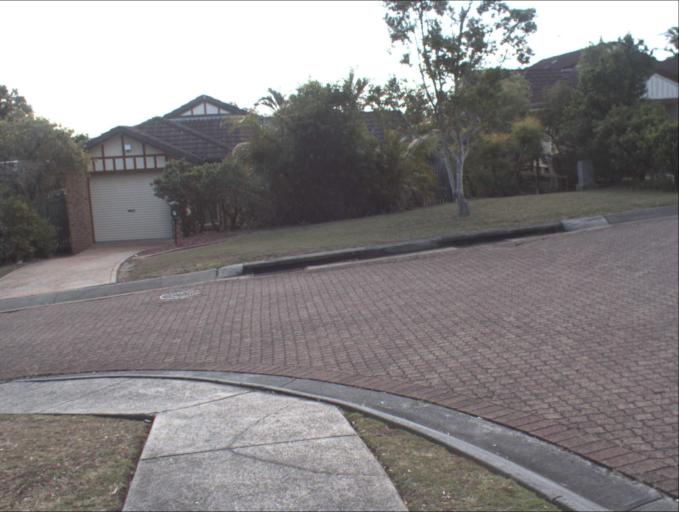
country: AU
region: Queensland
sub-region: Logan
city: Slacks Creek
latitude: -27.6327
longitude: 153.1465
